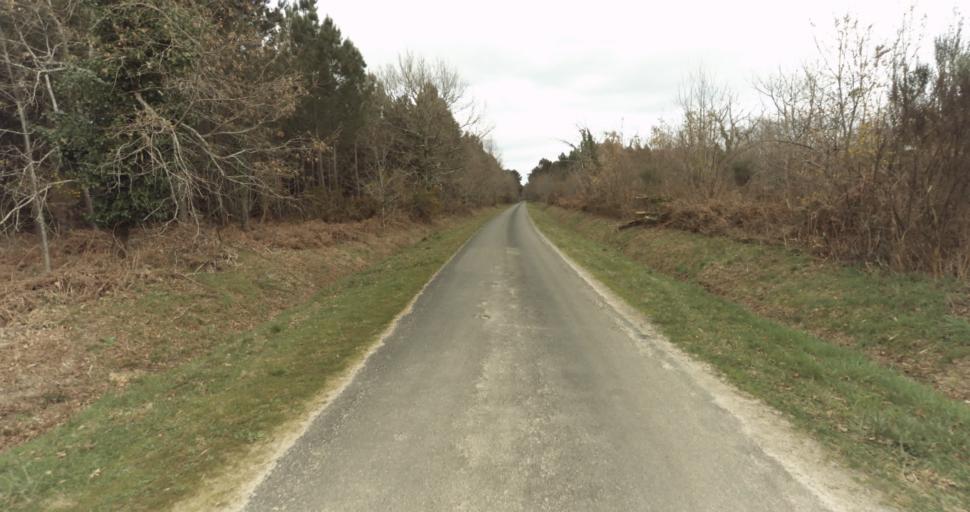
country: FR
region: Aquitaine
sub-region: Departement des Landes
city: Roquefort
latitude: 44.0649
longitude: -0.3878
